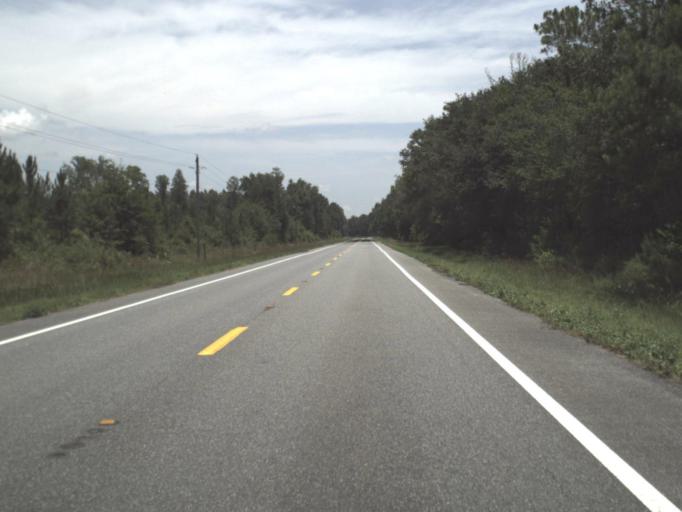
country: US
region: Florida
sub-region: Lafayette County
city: Mayo
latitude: 29.9819
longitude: -83.2008
